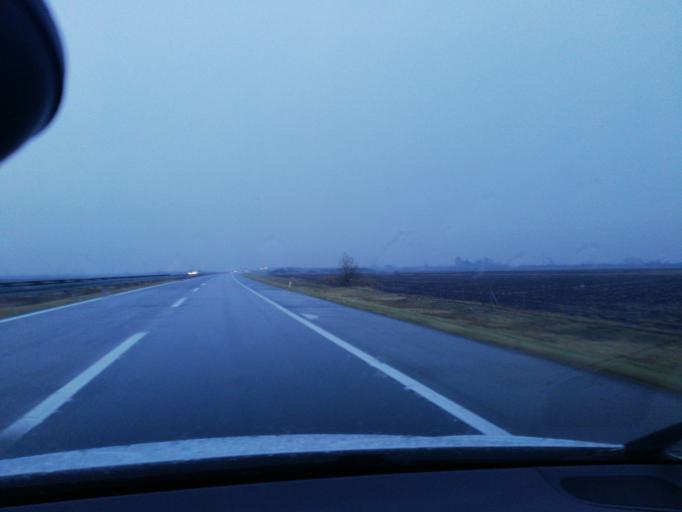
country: RS
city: Sasinci
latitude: 44.9812
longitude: 19.7261
